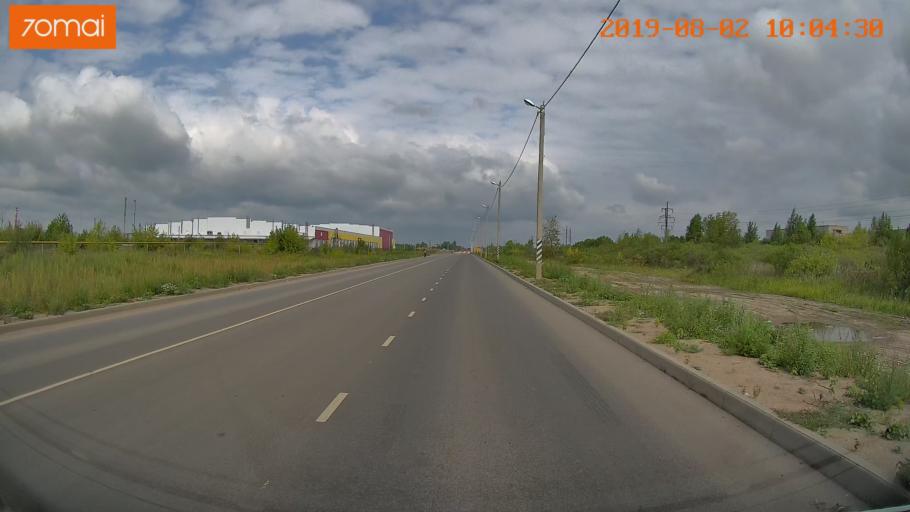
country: RU
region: Ivanovo
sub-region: Gorod Ivanovo
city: Ivanovo
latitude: 56.9726
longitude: 40.9256
